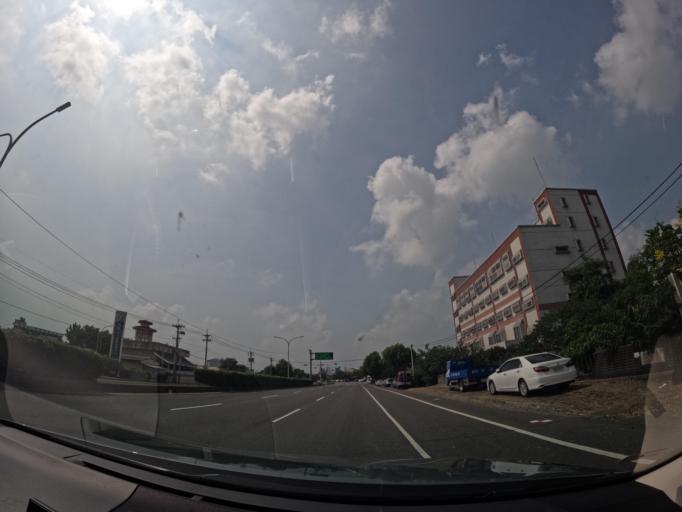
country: TW
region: Taiwan
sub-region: Yunlin
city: Douliu
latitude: 23.6964
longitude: 120.4810
